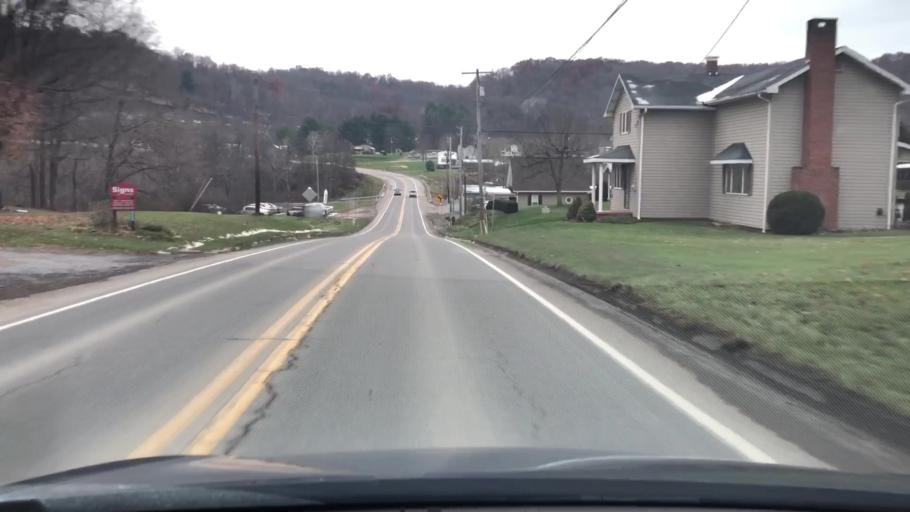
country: US
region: Pennsylvania
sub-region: Clarion County
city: Clarion
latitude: 41.0142
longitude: -79.2968
